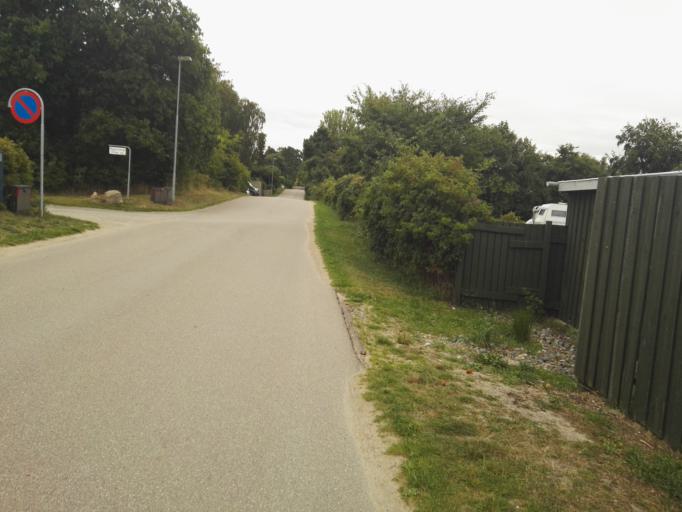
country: DK
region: Zealand
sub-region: Odsherred Kommune
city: Nykobing Sjaelland
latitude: 55.9385
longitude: 11.6637
